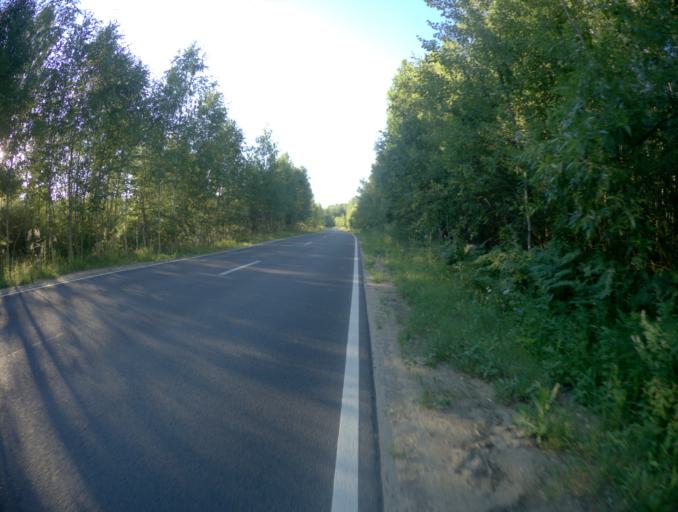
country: RU
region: Vladimir
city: Galitsy
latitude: 56.1329
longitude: 42.8741
